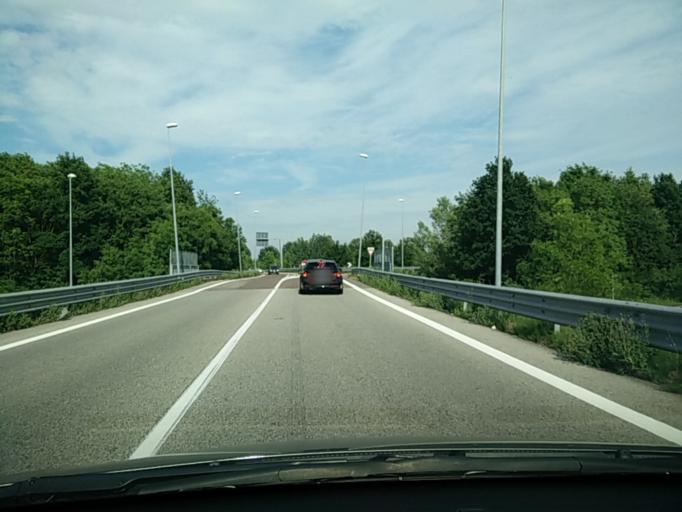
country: IT
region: Veneto
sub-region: Provincia di Venezia
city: Musile di Piave
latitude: 45.5920
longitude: 12.5521
